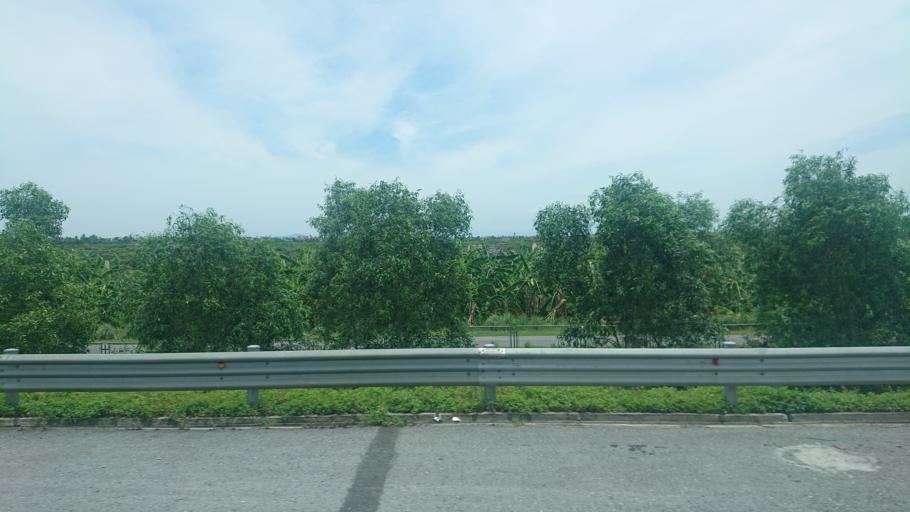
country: VN
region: Hai Duong
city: Tu Ky
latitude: 20.8235
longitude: 106.4693
